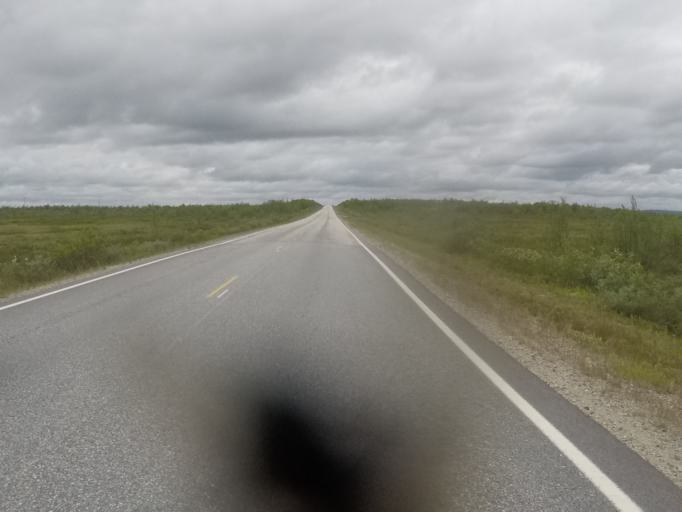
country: NO
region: Finnmark Fylke
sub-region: Kautokeino
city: Kautokeino
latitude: 68.7914
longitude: 23.2967
